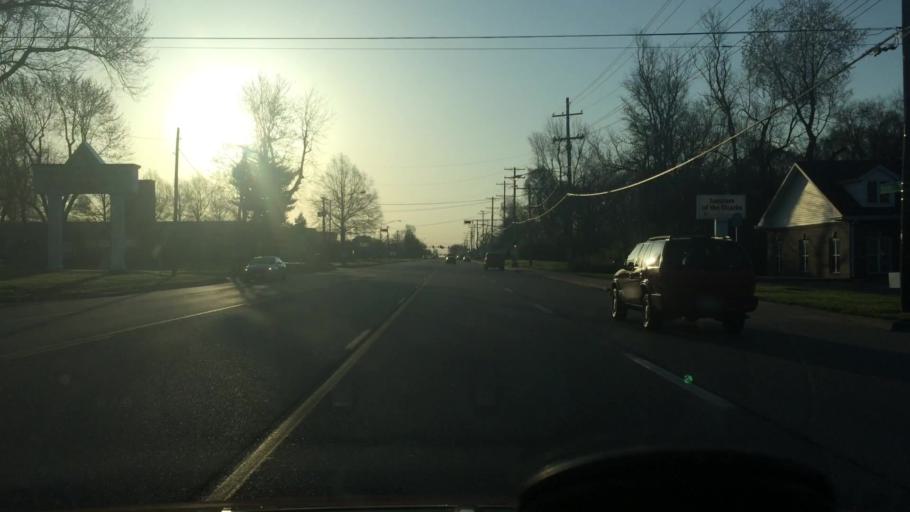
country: US
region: Missouri
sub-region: Greene County
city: Springfield
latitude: 37.1813
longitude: -93.2557
